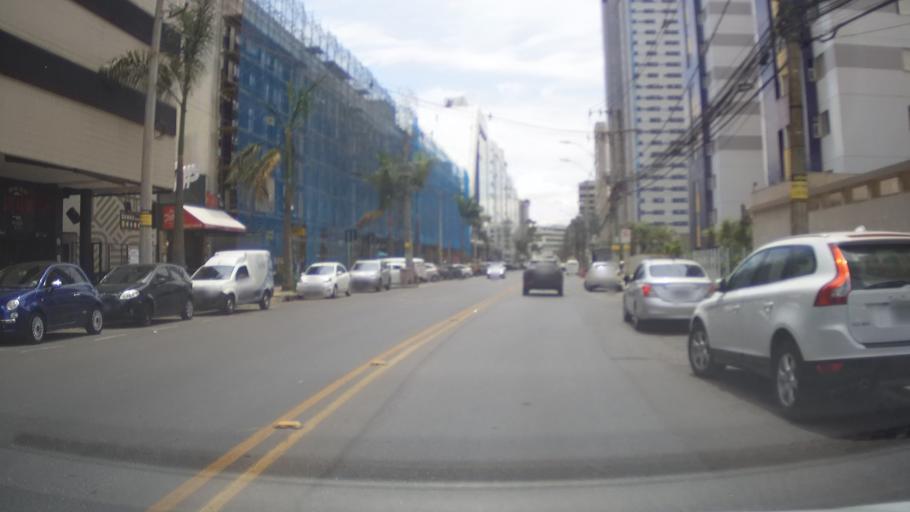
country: BR
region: Minas Gerais
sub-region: Belo Horizonte
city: Belo Horizonte
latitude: -19.9783
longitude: -43.9422
